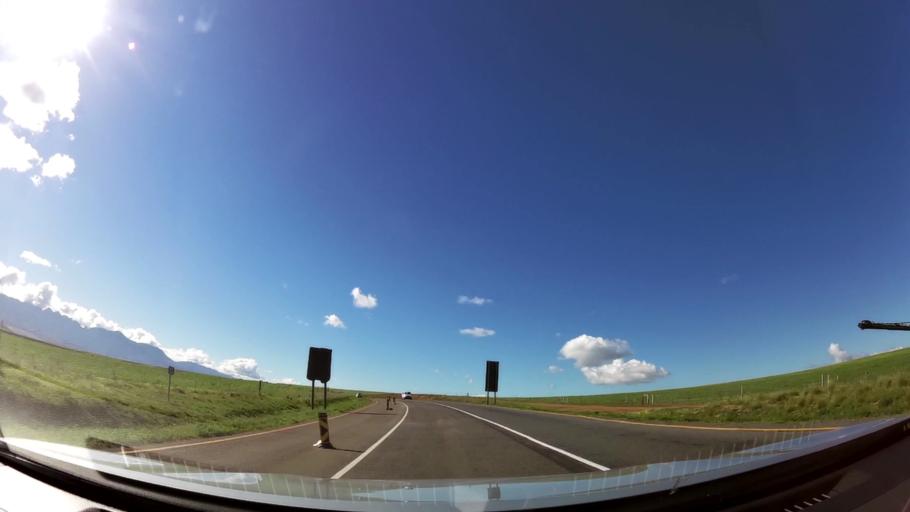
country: ZA
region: Western Cape
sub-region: Overberg District Municipality
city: Caledon
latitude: -34.1845
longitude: 19.6822
